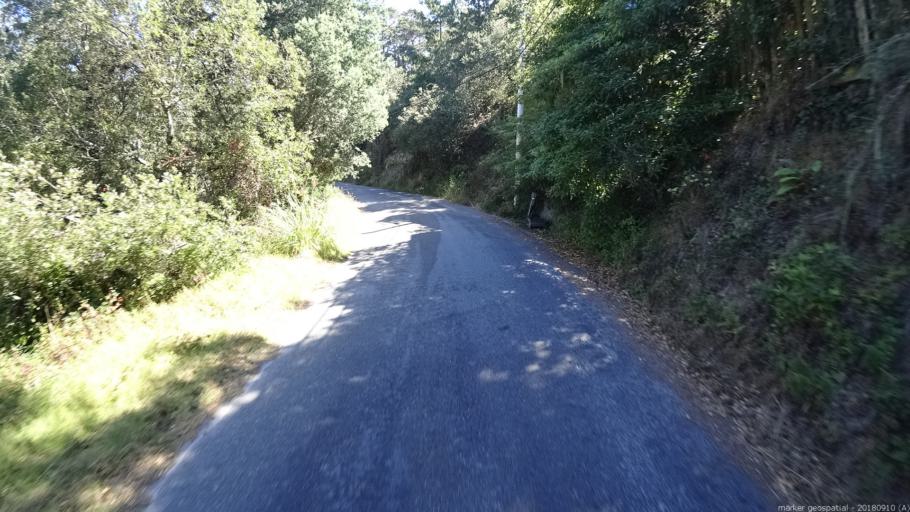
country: US
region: California
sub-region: Monterey County
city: Carmel-by-the-Sea
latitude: 36.5029
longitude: -121.9331
